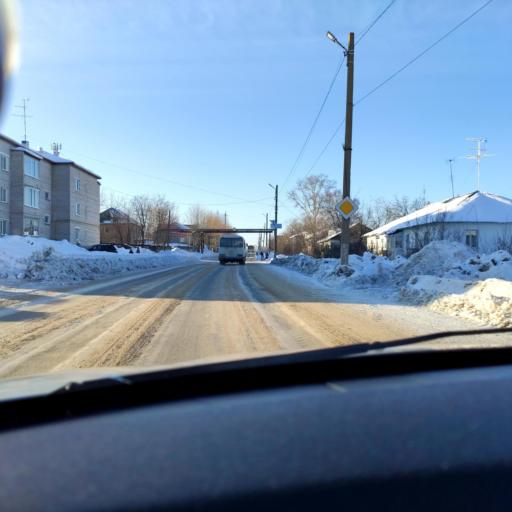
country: RU
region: Perm
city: Polazna
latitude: 58.2920
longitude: 56.4111
